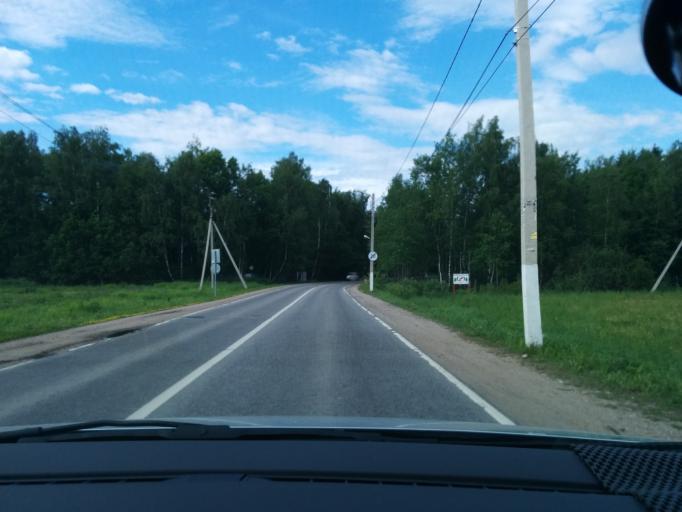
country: RU
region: Moskovskaya
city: Lugovaya
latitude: 56.0348
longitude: 37.4686
